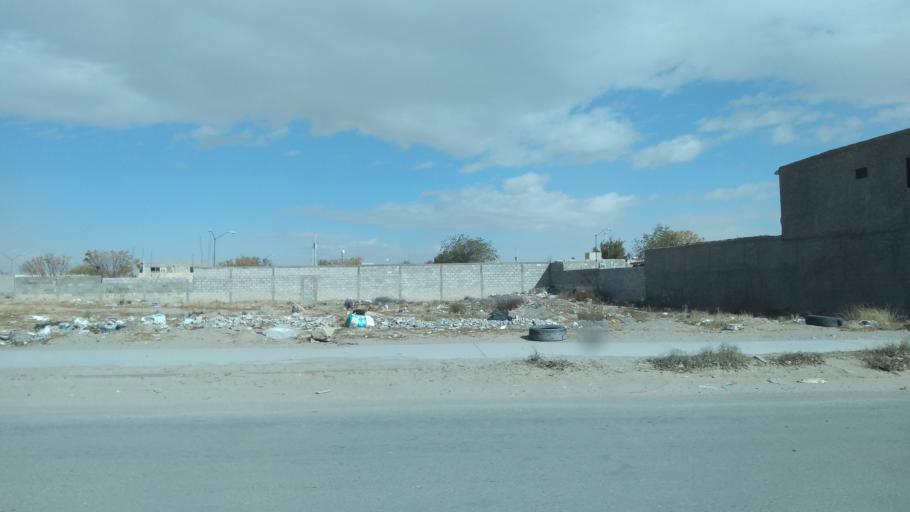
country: US
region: Texas
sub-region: El Paso County
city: San Elizario
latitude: 31.5668
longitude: -106.3402
